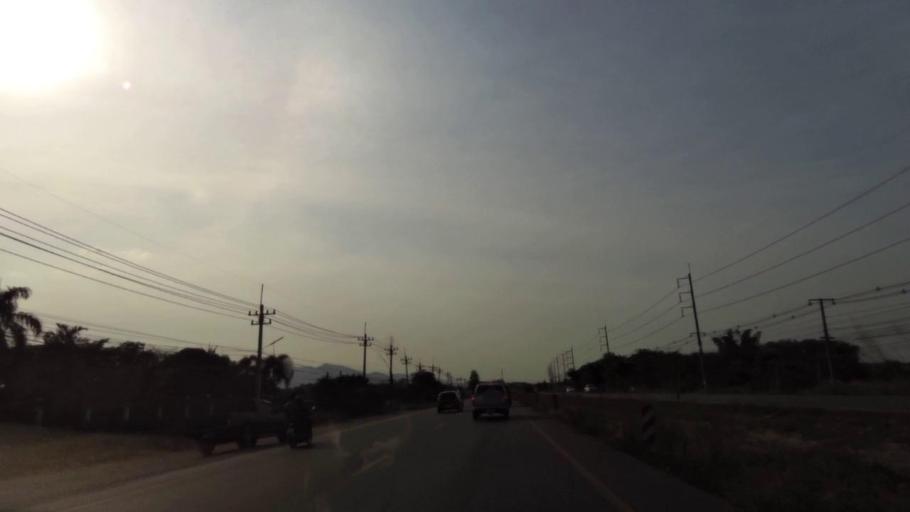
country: TH
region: Chon Buri
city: Ban Bueng
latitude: 13.2993
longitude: 101.1535
